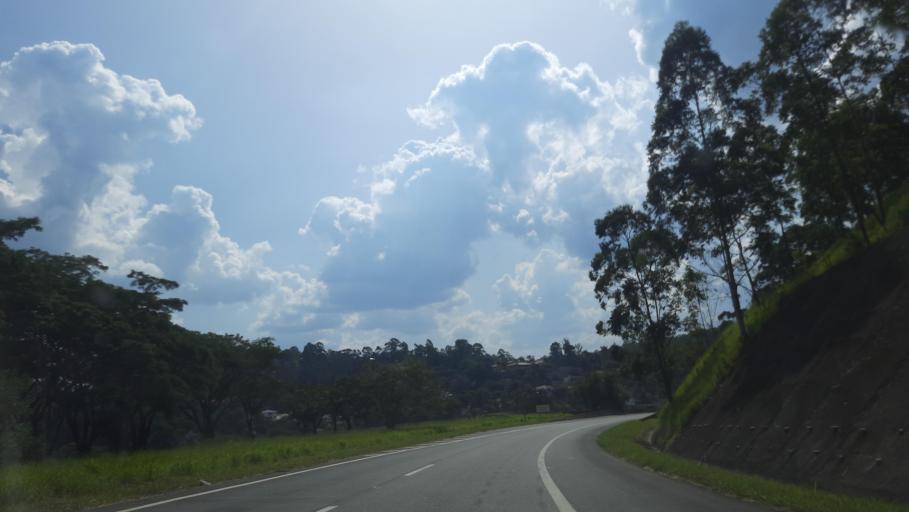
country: BR
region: Sao Paulo
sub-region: Caieiras
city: Caieiras
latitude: -23.4312
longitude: -46.7580
